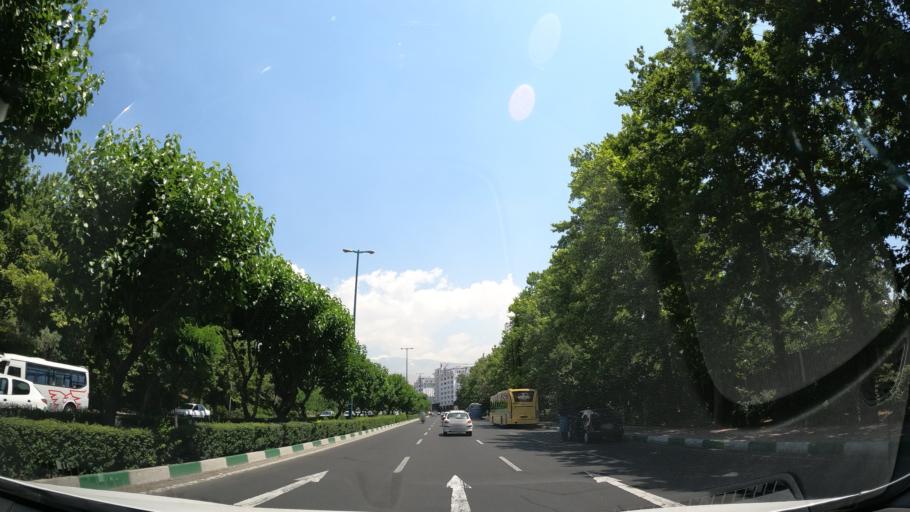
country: IR
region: Tehran
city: Tajrish
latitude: 35.7651
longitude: 51.3777
